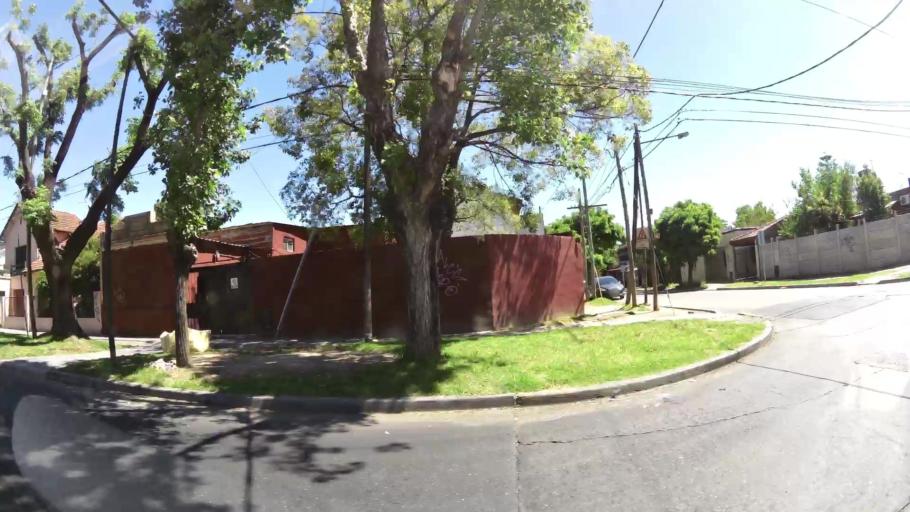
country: AR
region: Buenos Aires
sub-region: Partido de San Isidro
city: San Isidro
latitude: -34.5113
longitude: -58.5647
